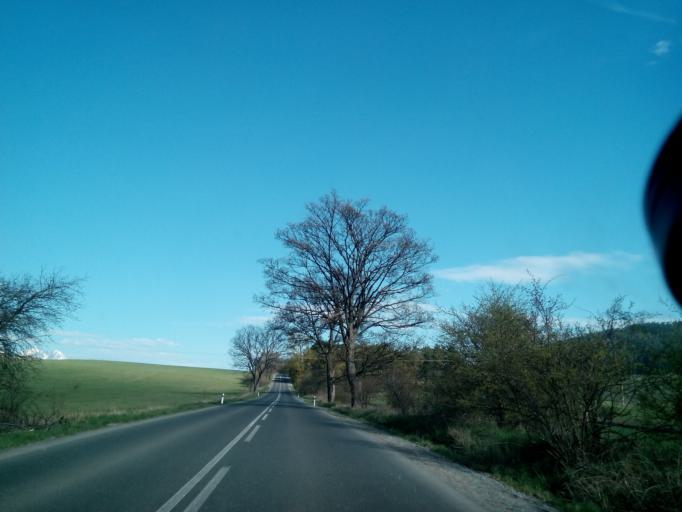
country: SK
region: Presovsky
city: Lubica
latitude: 49.0239
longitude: 20.4401
